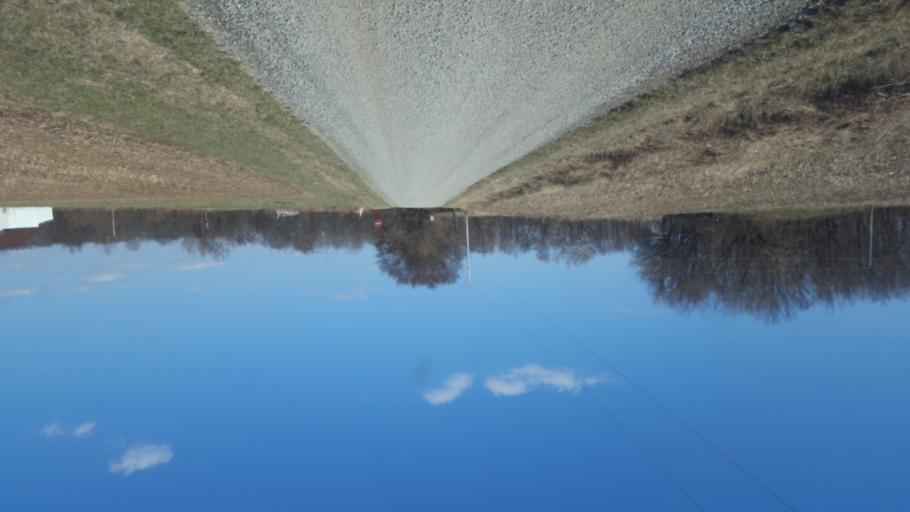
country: US
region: Ohio
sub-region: Morrow County
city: Mount Gilead
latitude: 40.4734
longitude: -82.7443
